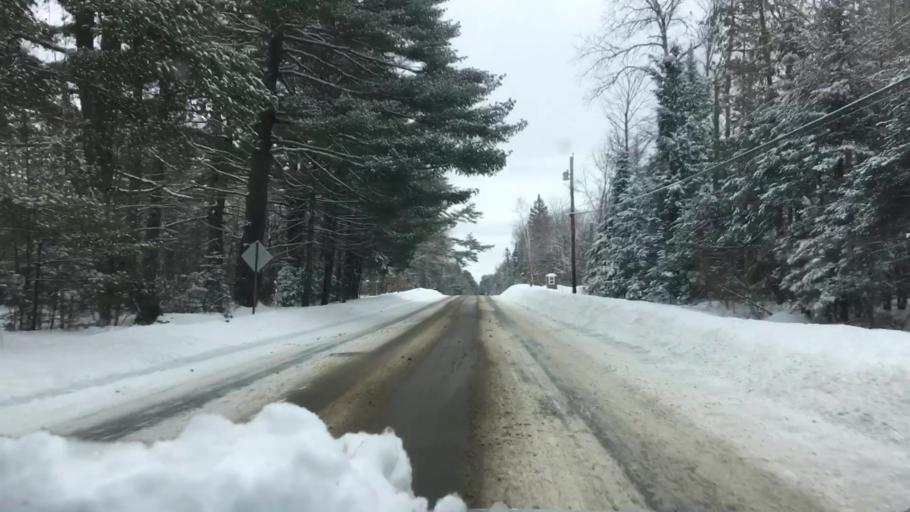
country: US
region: Maine
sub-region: Penobscot County
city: Hudson
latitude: 45.0207
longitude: -68.9122
